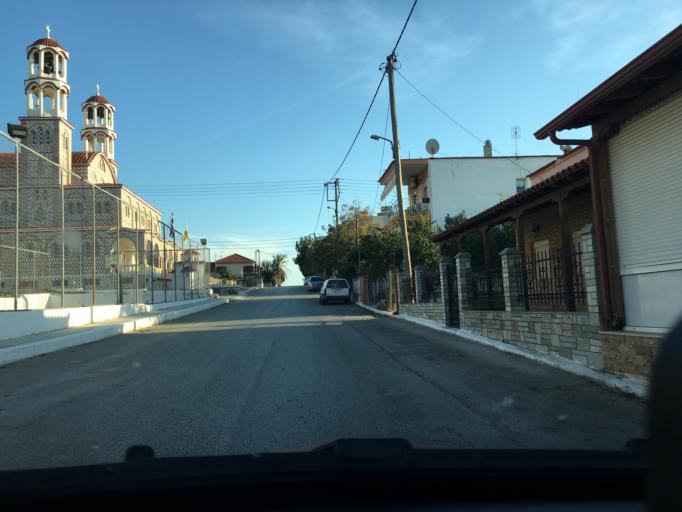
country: GR
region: Central Macedonia
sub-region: Nomos Chalkidikis
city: Nea Poteidaia
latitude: 40.1938
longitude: 23.3275
